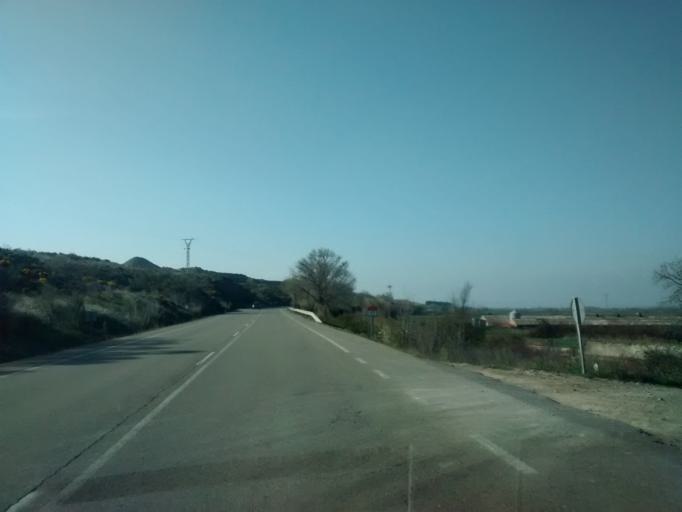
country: ES
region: Aragon
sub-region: Provincia de Zaragoza
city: San Mateo de Gallego
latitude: 41.8063
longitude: -0.7768
